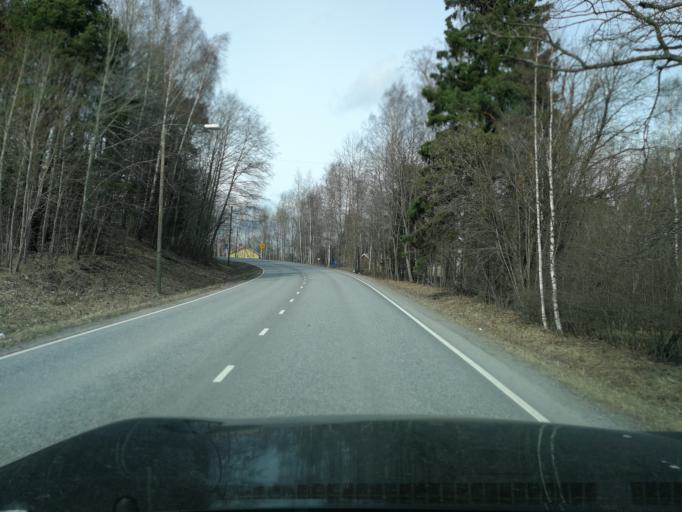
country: FI
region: Uusimaa
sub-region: Helsinki
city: Siuntio
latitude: 60.1307
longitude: 24.2324
